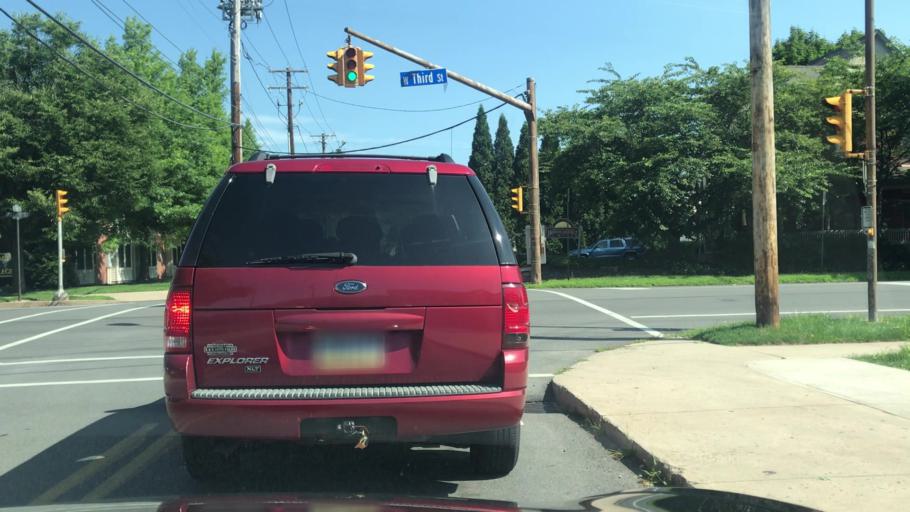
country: US
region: Pennsylvania
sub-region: Lycoming County
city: Duboistown
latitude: 41.2374
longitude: -77.0229
